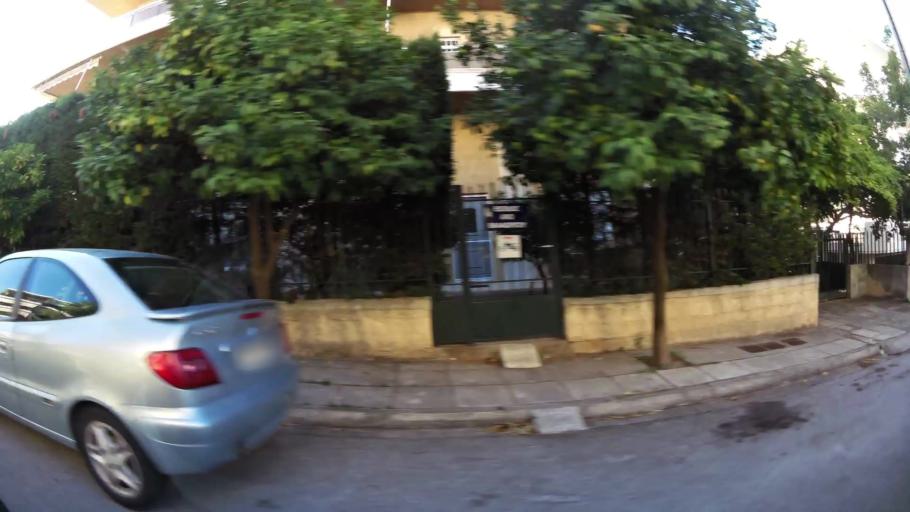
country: GR
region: Attica
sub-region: Nomarchia Athinas
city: Glyfada
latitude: 37.8756
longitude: 23.7619
